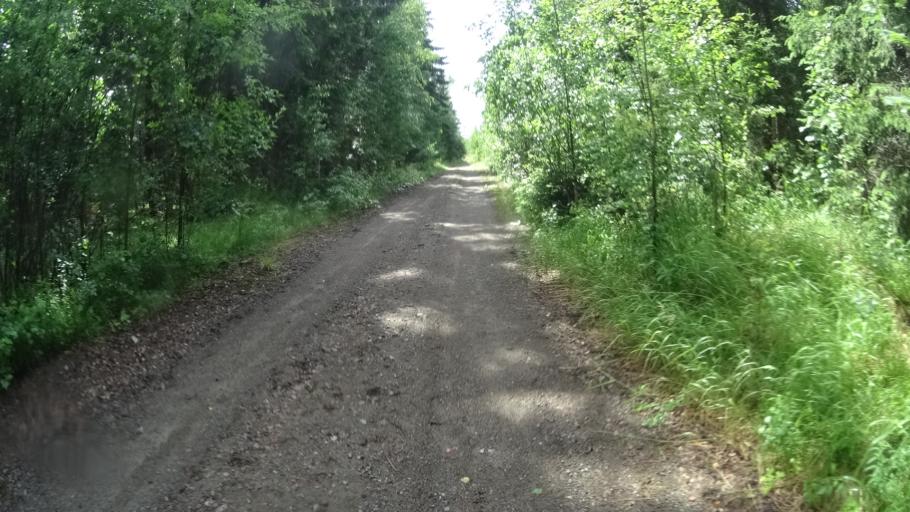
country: FI
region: Uusimaa
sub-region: Helsinki
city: Karkkila
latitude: 60.5877
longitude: 24.3333
